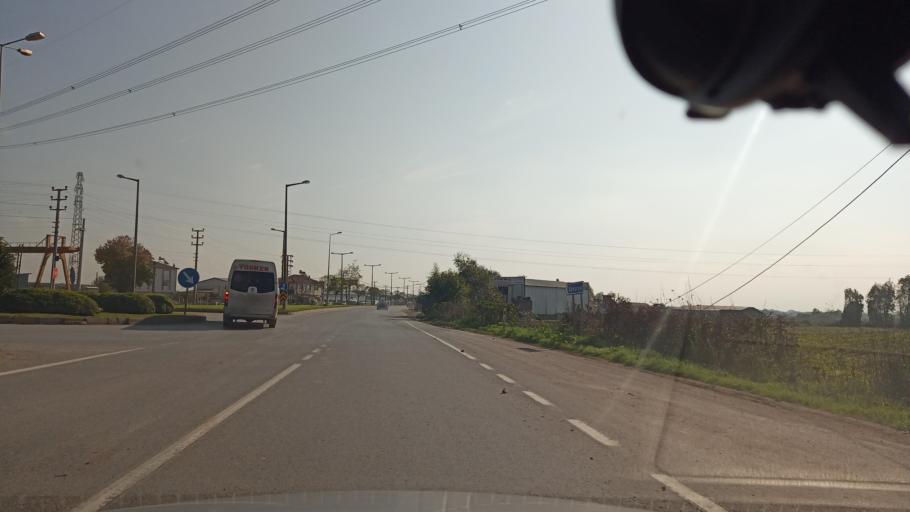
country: TR
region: Sakarya
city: Adapazari
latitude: 40.8217
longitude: 30.3966
